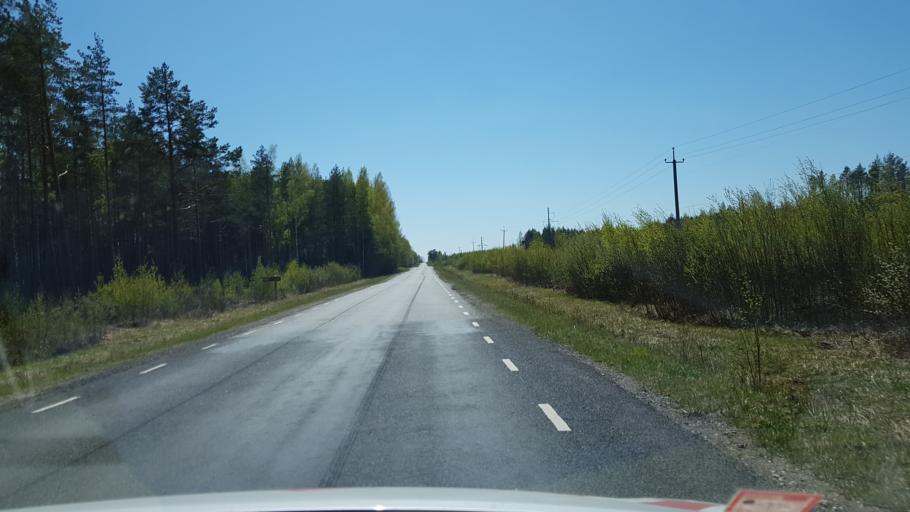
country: EE
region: Vorumaa
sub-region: Voru linn
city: Voru
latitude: 57.9371
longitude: 26.9526
